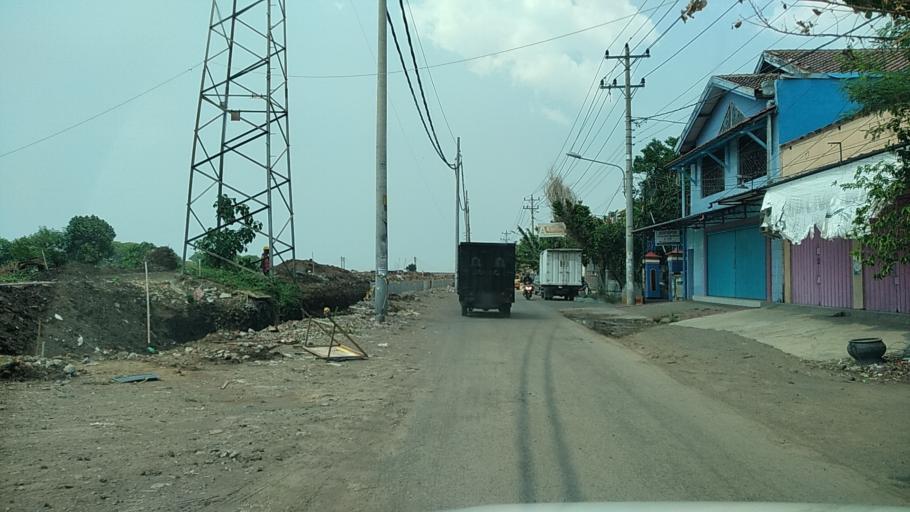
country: ID
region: Central Java
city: Semarang
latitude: -6.9914
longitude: 110.4407
